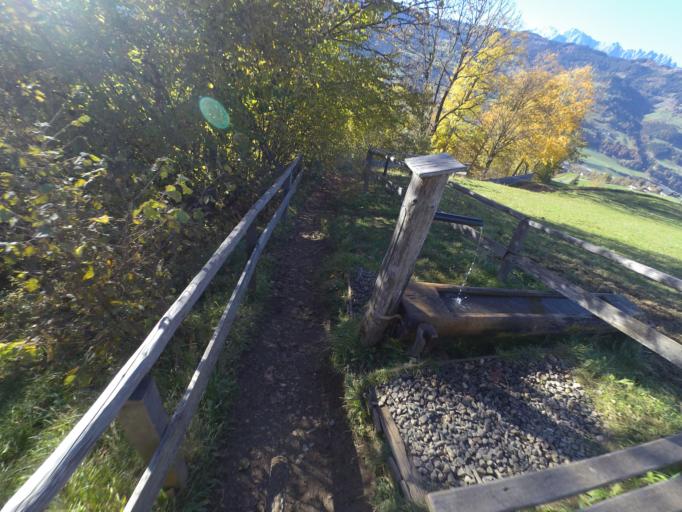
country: AT
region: Salzburg
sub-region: Politischer Bezirk Sankt Johann im Pongau
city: Sankt Johann im Pongau
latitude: 47.3457
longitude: 13.2192
